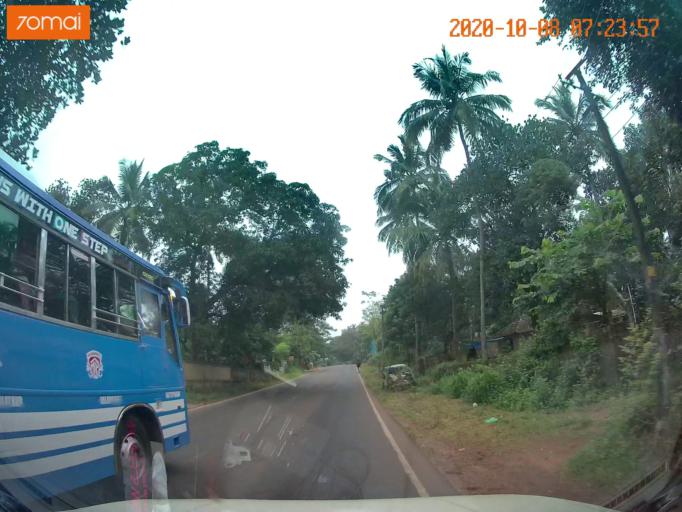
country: IN
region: Kerala
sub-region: Malappuram
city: Tirur
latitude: 10.8682
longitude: 76.0491
